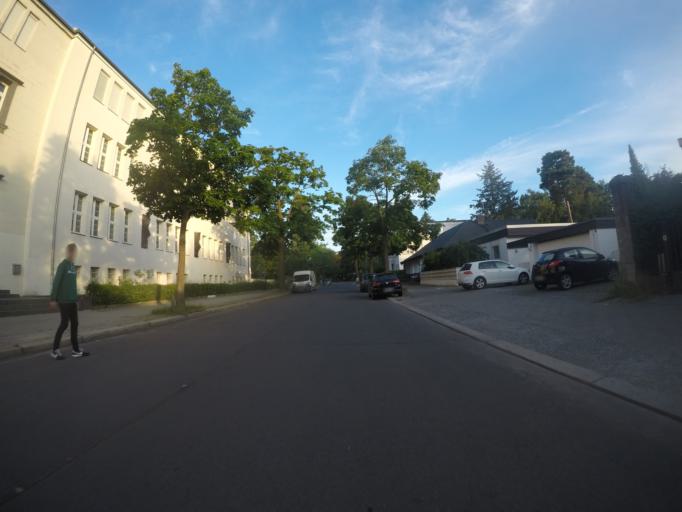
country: DE
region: Berlin
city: Halensee
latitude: 52.4913
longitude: 13.2810
